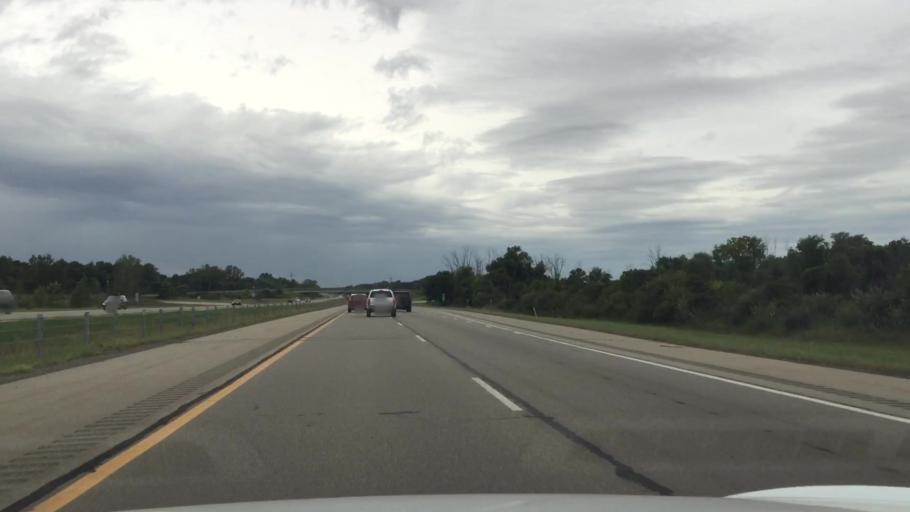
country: US
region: Michigan
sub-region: Macomb County
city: New Baltimore
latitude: 42.7240
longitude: -82.7475
